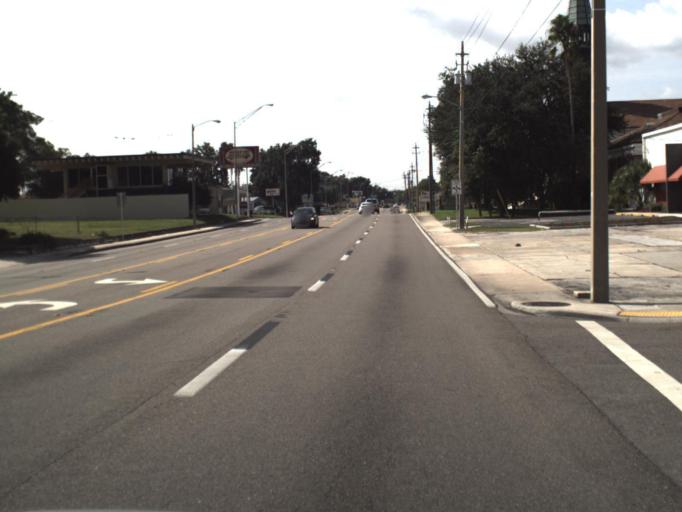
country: US
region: Florida
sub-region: Polk County
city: Winter Haven
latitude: 28.0295
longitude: -81.7330
